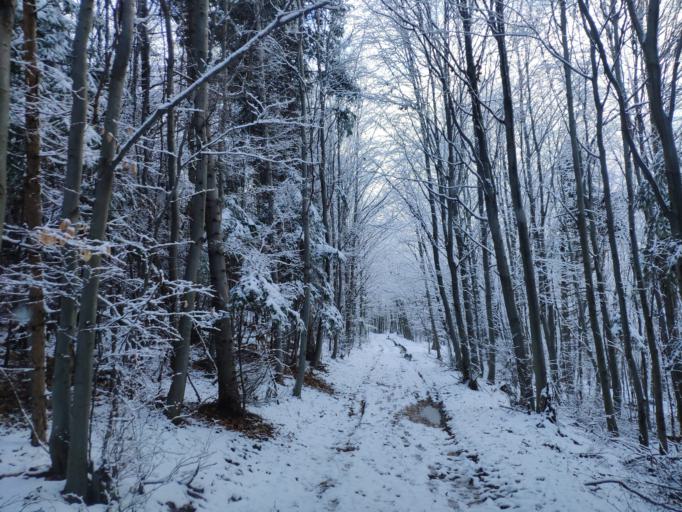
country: SK
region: Kosicky
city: Moldava nad Bodvou
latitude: 48.7444
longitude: 21.0897
